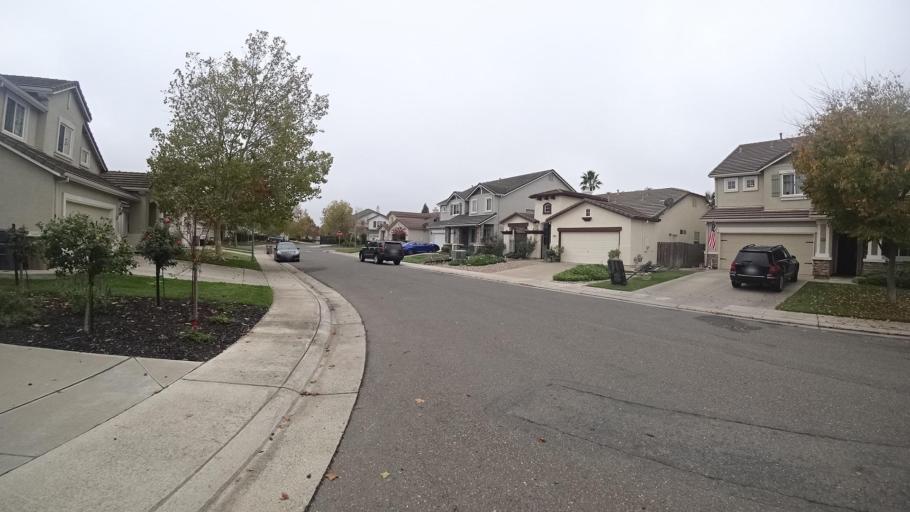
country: US
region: California
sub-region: Sacramento County
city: Elk Grove
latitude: 38.4053
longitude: -121.3454
